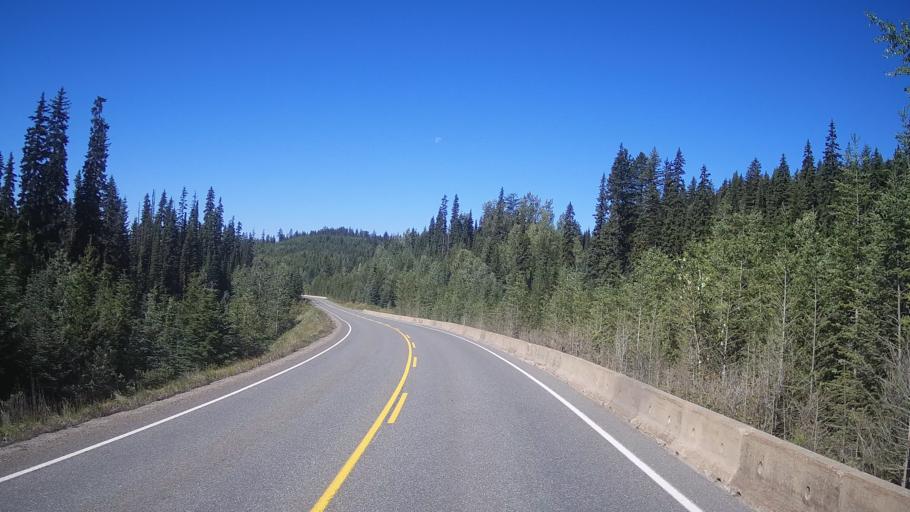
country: CA
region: British Columbia
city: Kamloops
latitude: 51.4992
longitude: -120.4436
